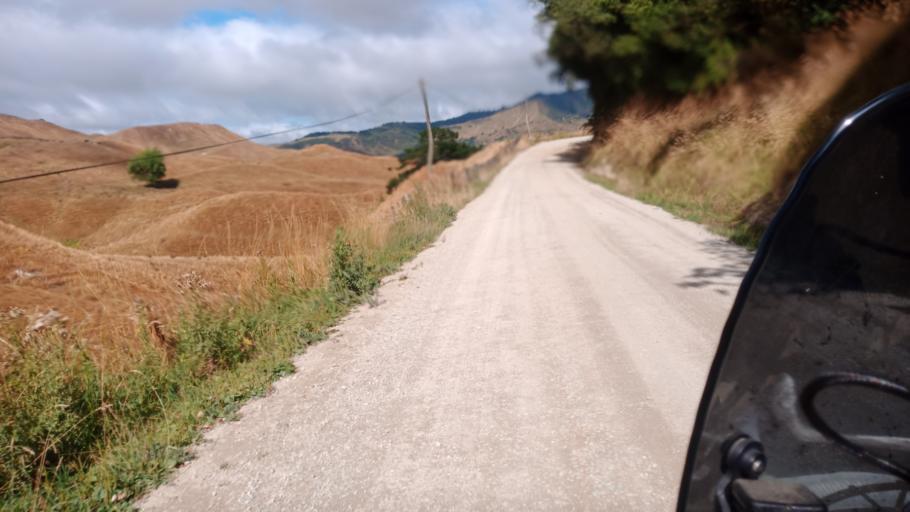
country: NZ
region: Hawke's Bay
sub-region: Wairoa District
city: Wairoa
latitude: -38.6072
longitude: 177.4573
